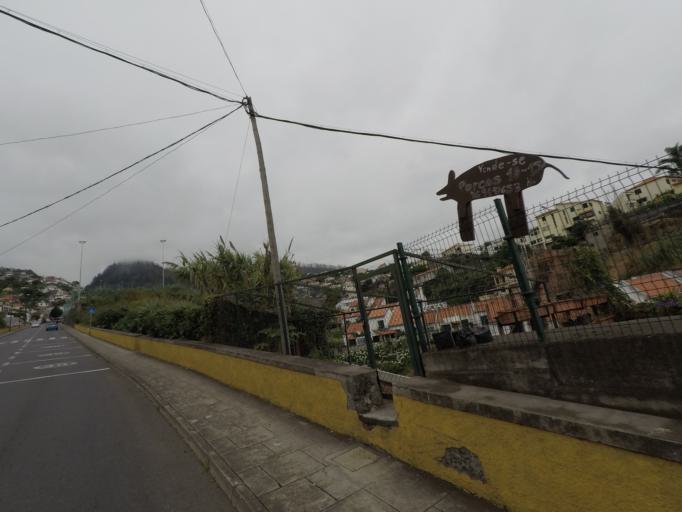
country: PT
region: Madeira
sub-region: Funchal
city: Nossa Senhora do Monte
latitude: 32.6685
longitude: -16.9368
